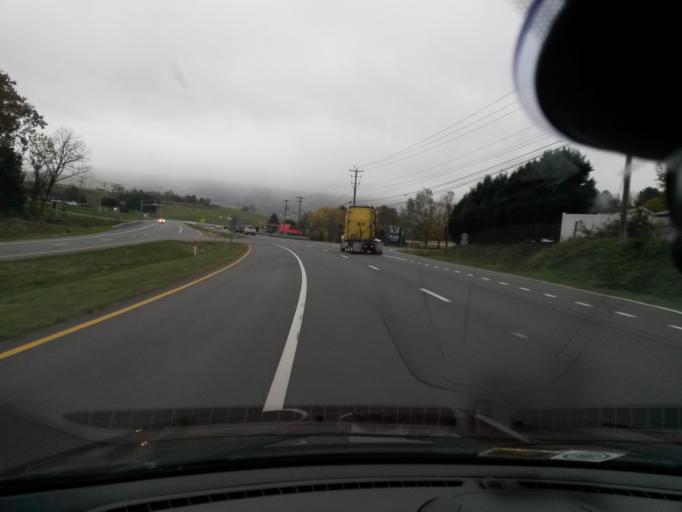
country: US
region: Virginia
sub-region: Botetourt County
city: Laymantown
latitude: 37.3436
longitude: -79.8806
